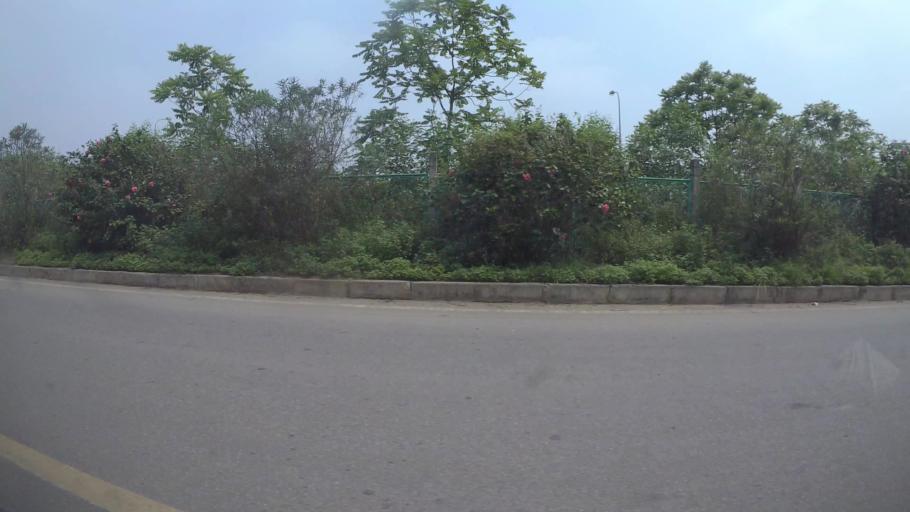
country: VN
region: Ha Noi
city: Lien Quan
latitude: 20.9899
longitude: 105.5510
